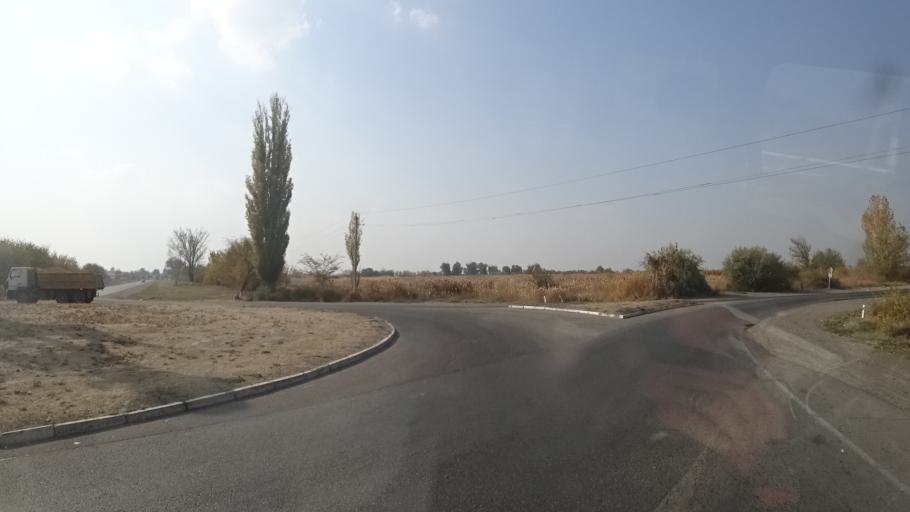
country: KZ
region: Zhambyl
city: Sarykemer
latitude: 42.9375
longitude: 71.4435
